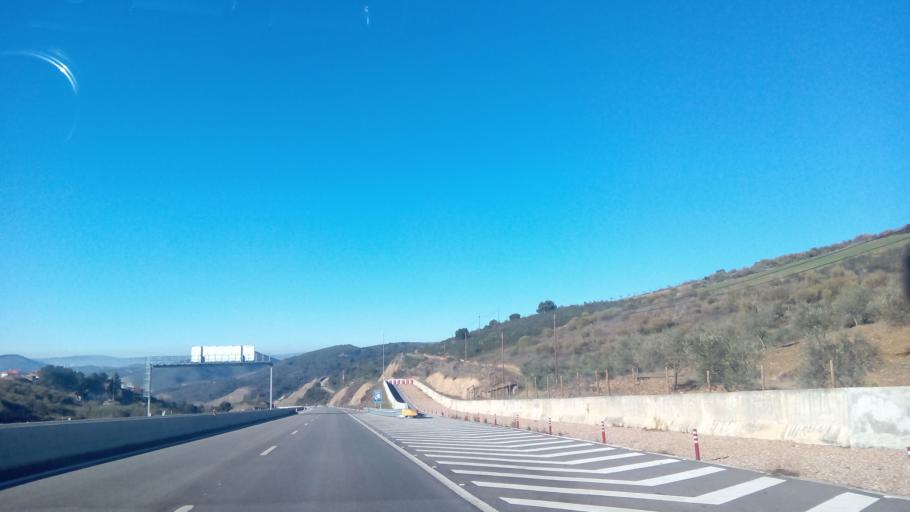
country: PT
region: Braganca
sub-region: Braganca Municipality
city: Braganca
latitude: 41.7604
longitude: -6.6474
